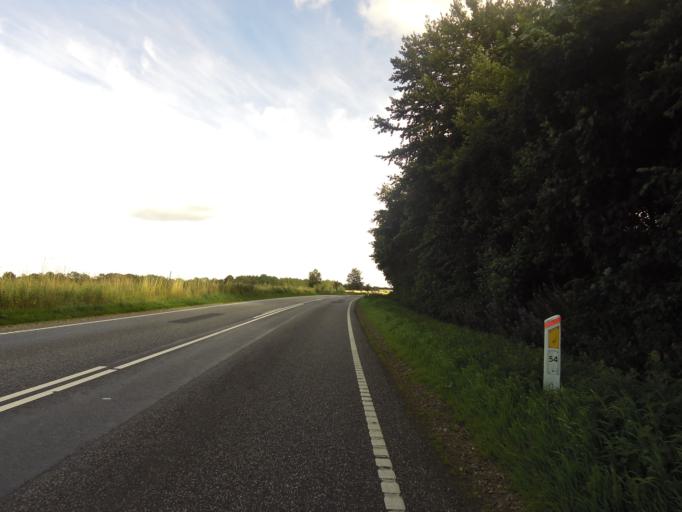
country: DK
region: South Denmark
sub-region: Tonder Kommune
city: Toftlund
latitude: 55.2164
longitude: 9.0302
